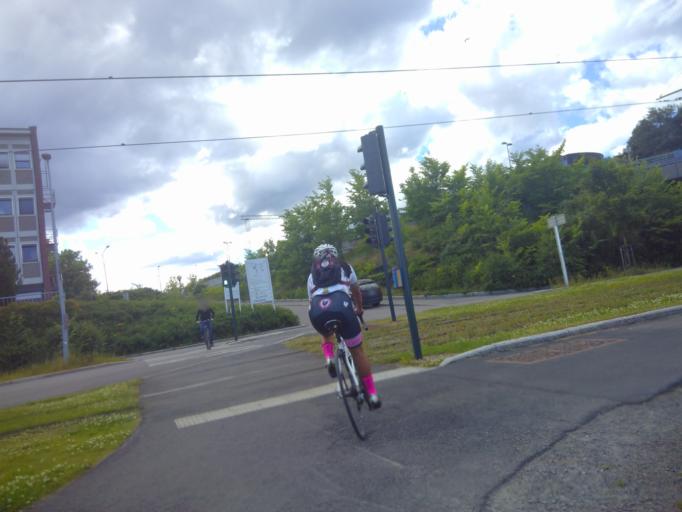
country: NO
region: Oslo
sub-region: Oslo
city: Oslo
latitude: 59.9451
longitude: 10.7175
